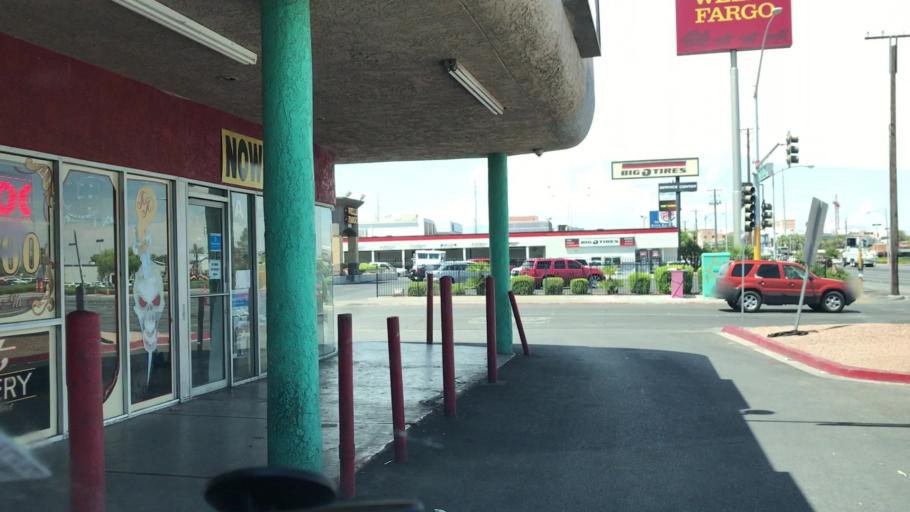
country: US
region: Nevada
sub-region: Clark County
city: Winchester
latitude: 36.1267
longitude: -115.1374
